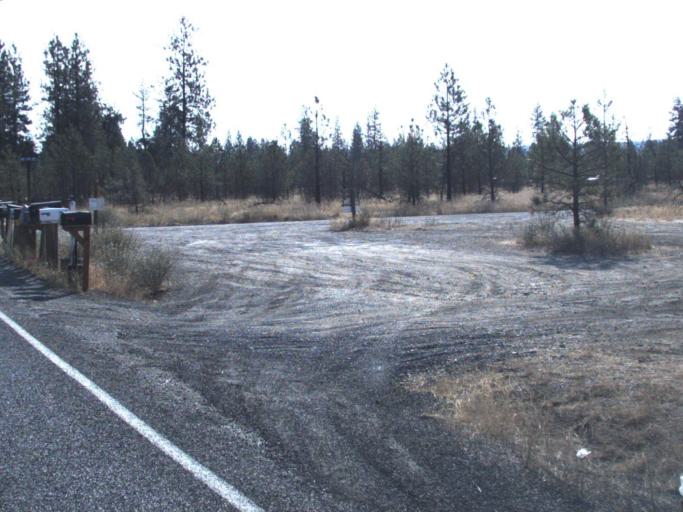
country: US
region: Washington
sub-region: Spokane County
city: Fairchild Air Force Base
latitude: 47.8393
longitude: -117.7984
